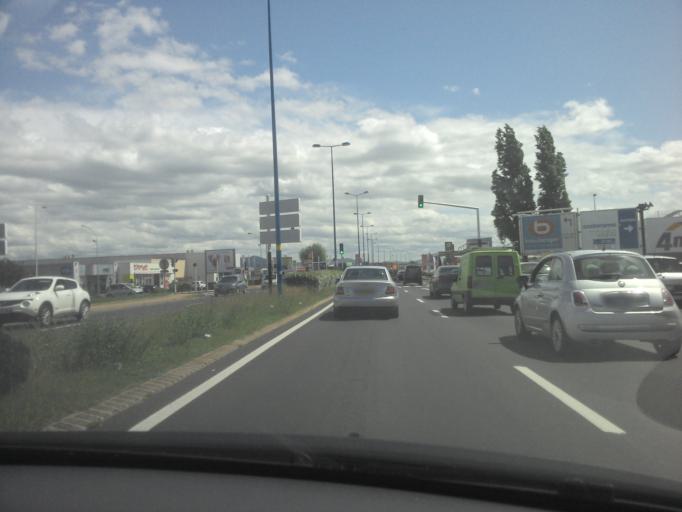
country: FR
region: Auvergne
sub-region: Departement du Puy-de-Dome
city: Aubiere
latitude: 45.7560
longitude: 3.1286
